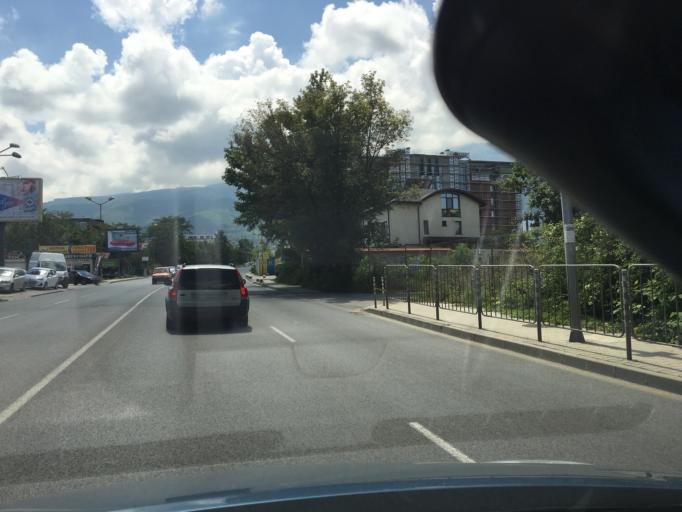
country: BG
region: Sofia-Capital
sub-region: Stolichna Obshtina
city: Sofia
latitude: 42.6457
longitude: 23.3143
